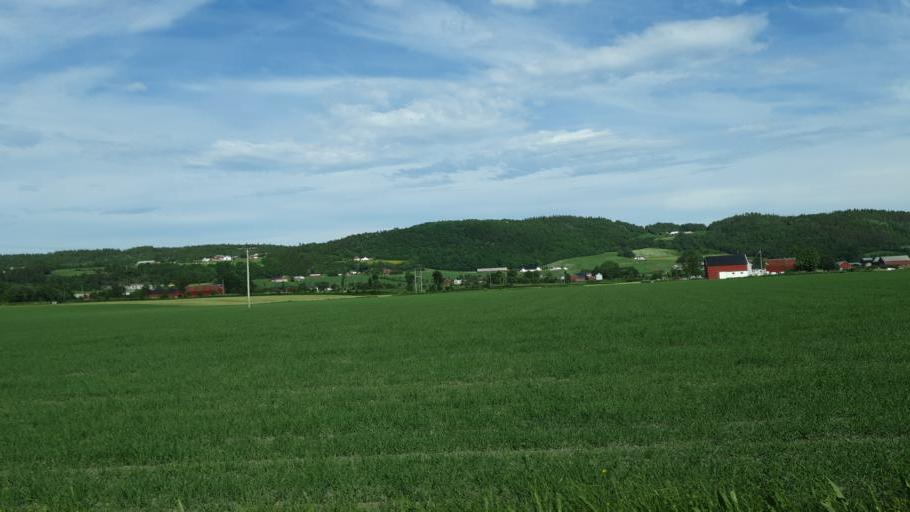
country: NO
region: Sor-Trondelag
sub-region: Rissa
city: Rissa
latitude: 63.4998
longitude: 10.0083
